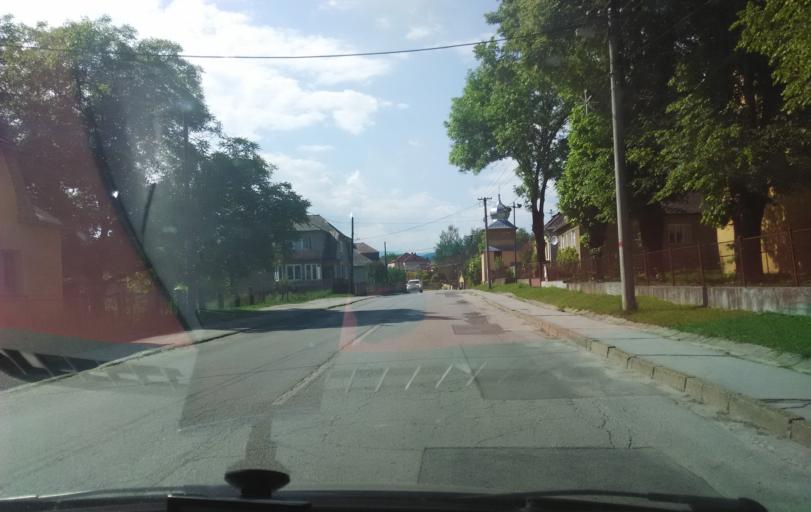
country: SK
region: Banskobystricky
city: Revuca
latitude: 48.6565
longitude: 20.1920
